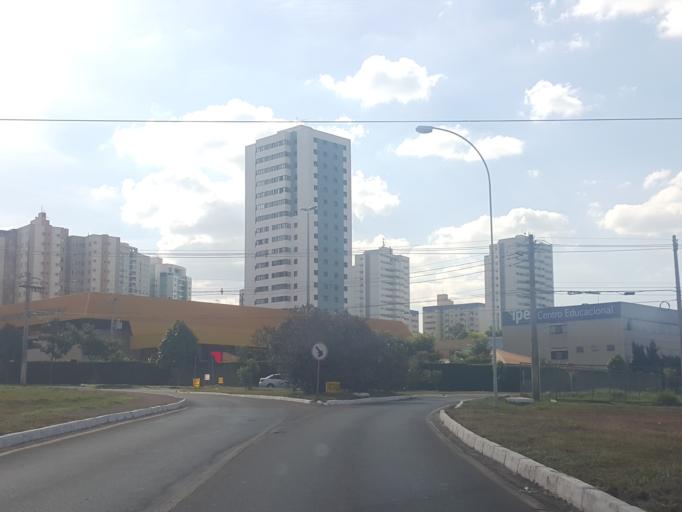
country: BR
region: Federal District
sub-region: Brasilia
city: Brasilia
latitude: -15.8384
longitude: -48.0083
